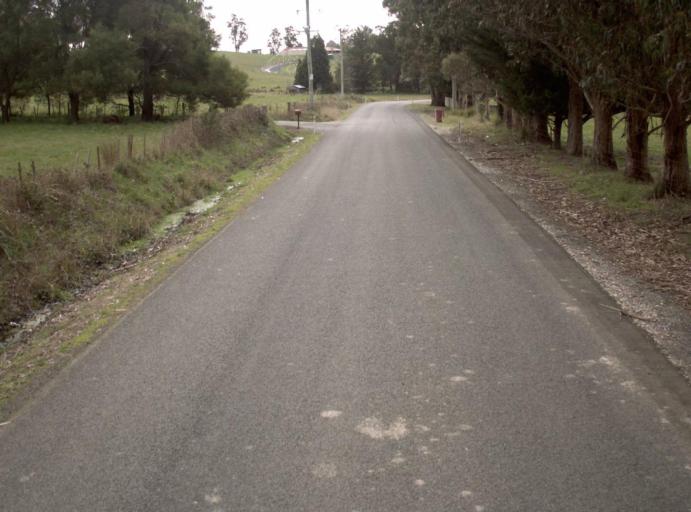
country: AU
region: Tasmania
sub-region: Launceston
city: Mayfield
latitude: -41.2676
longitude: 147.1608
